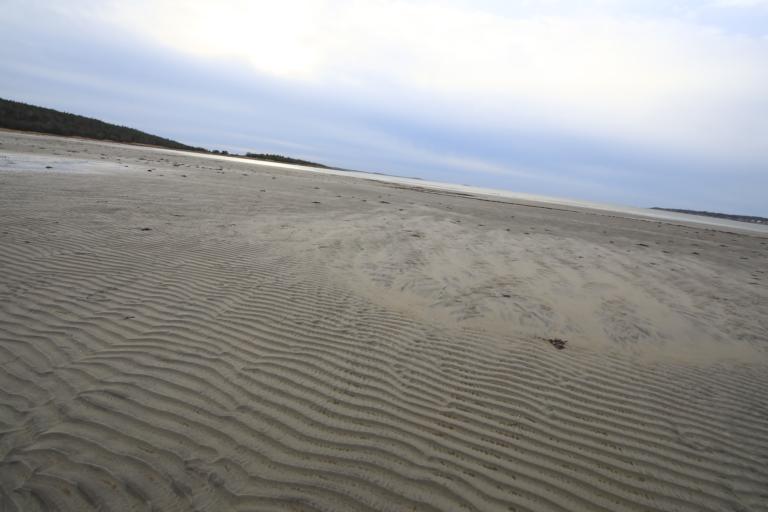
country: SE
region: Halland
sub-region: Varbergs Kommun
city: Varberg
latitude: 57.1842
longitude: 12.2128
